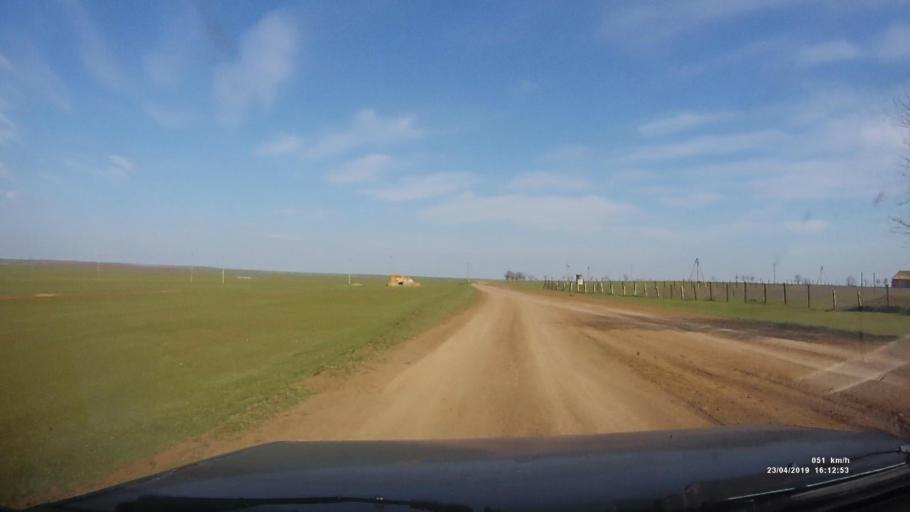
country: RU
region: Kalmykiya
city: Priyutnoye
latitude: 46.4648
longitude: 43.1311
